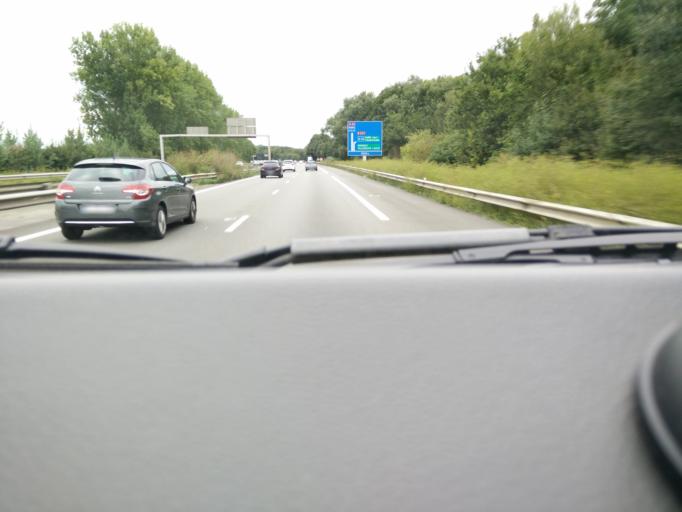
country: FR
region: Nord-Pas-de-Calais
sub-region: Departement du Nord
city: Sainghin-en-Melantois
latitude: 50.5879
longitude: 3.1494
